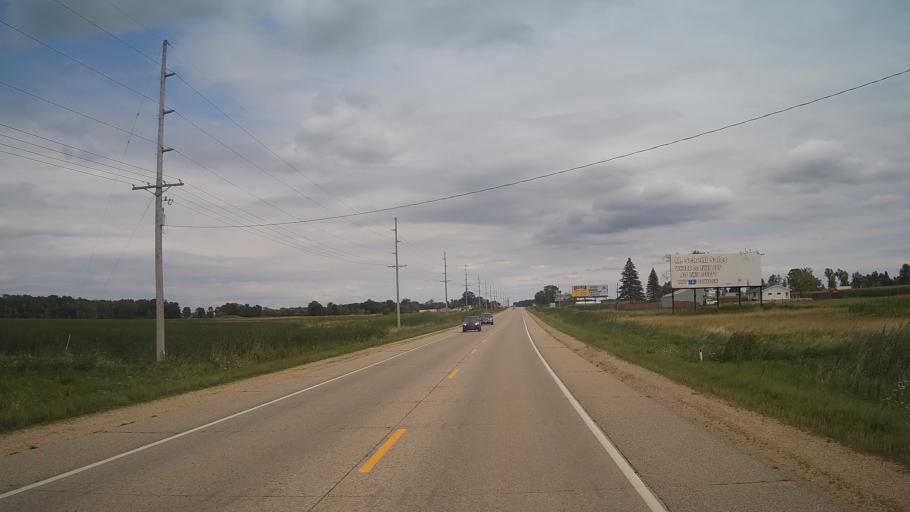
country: US
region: Wisconsin
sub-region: Waushara County
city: Redgranite
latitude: 44.0413
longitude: -89.0255
